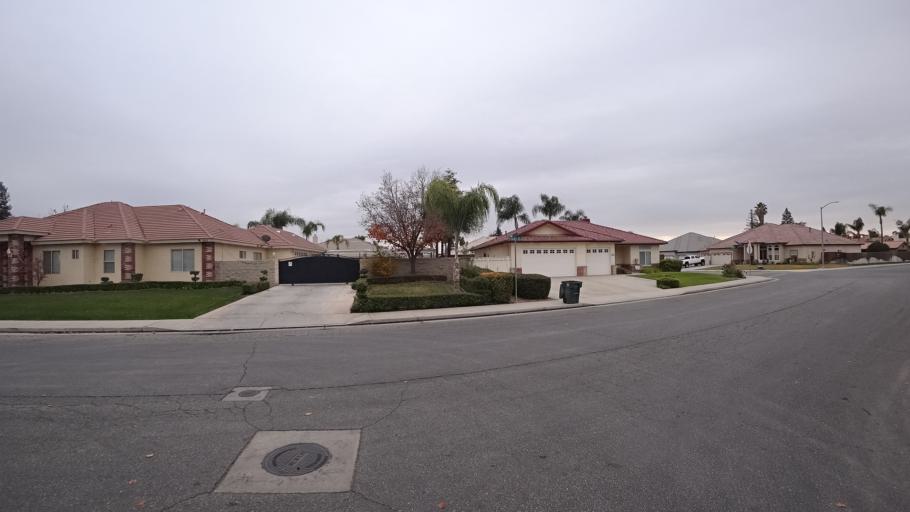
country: US
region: California
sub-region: Kern County
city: Greenfield
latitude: 35.2872
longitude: -119.0425
